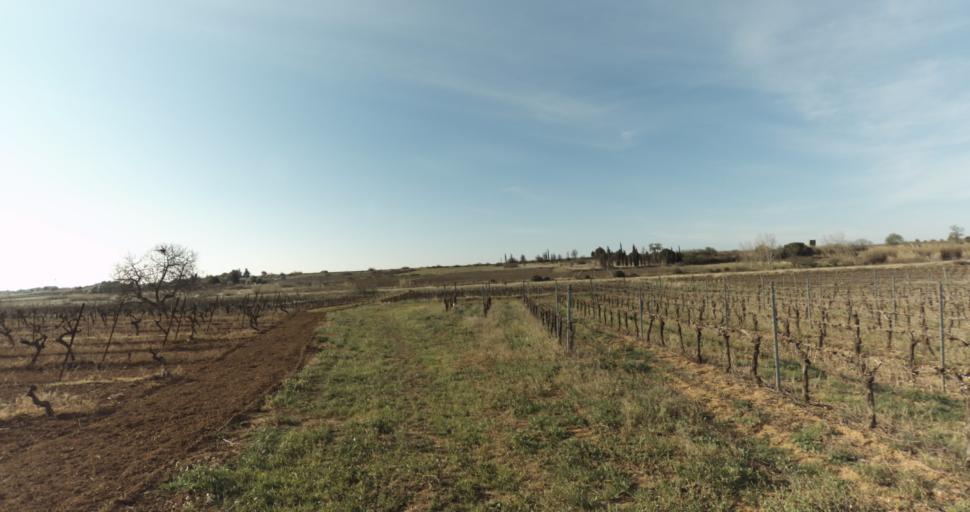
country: FR
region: Languedoc-Roussillon
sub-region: Departement de l'Herault
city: Marseillan
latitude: 43.3685
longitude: 3.5086
